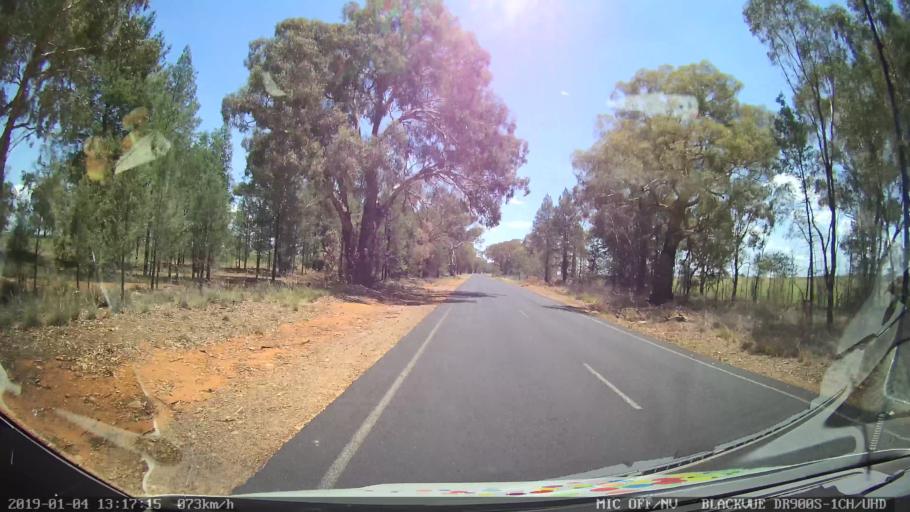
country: AU
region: New South Wales
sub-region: Wellington
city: Wellington
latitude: -32.7519
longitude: 148.6357
